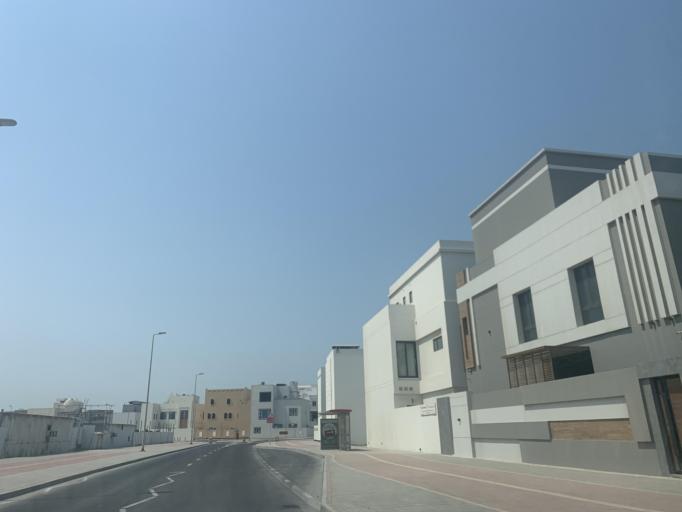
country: BH
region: Muharraq
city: Al Hadd
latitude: 26.2383
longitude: 50.6614
